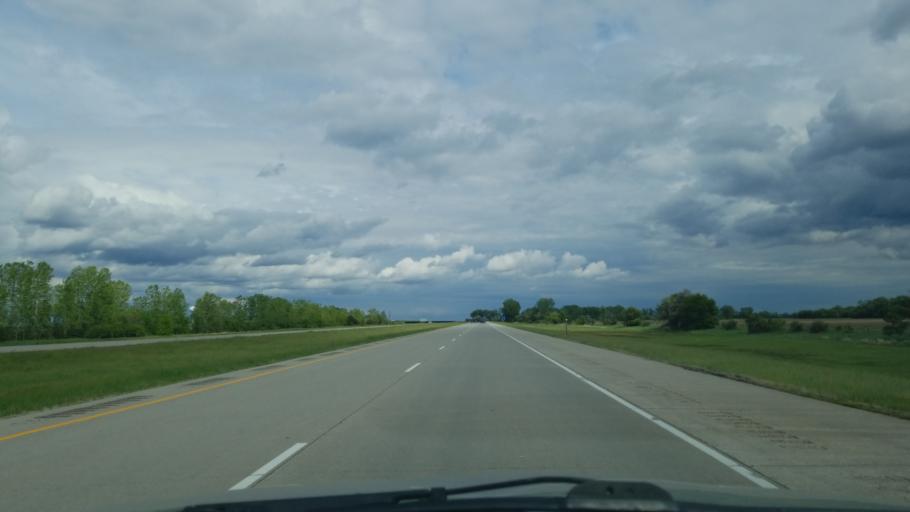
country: US
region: North Dakota
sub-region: Cass County
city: Casselton
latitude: 46.8754
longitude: -97.2345
